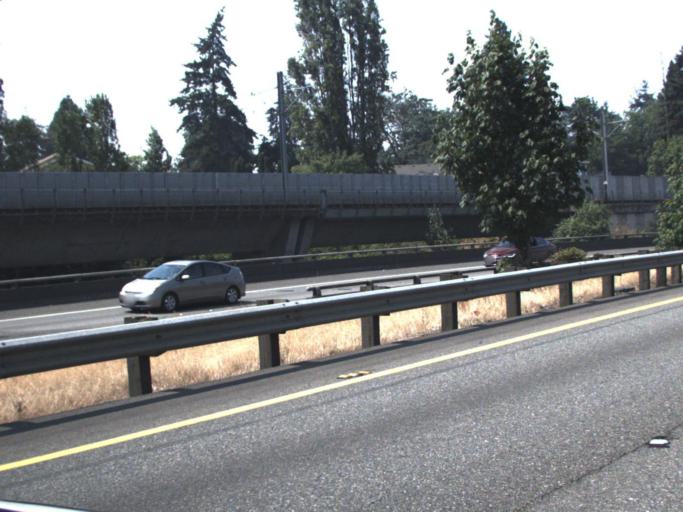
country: US
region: Washington
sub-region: King County
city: Riverton
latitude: 47.4888
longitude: -122.2800
